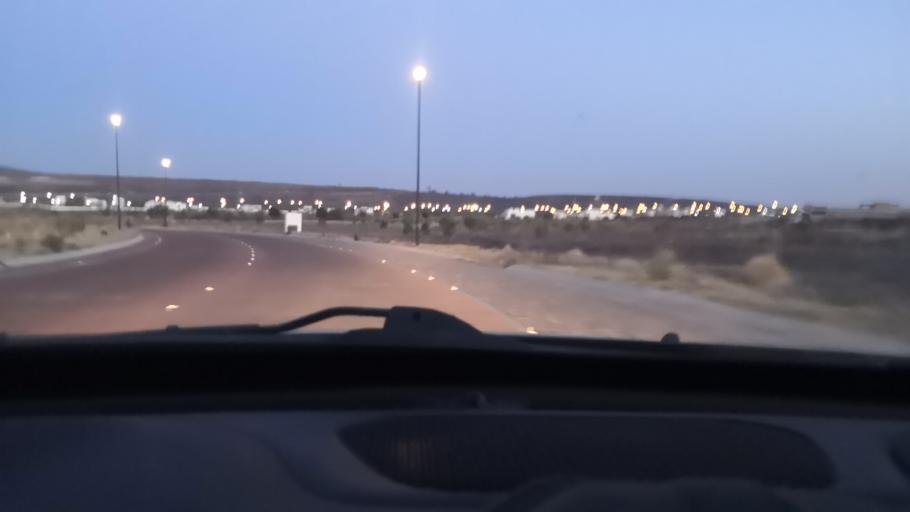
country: MX
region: Guanajuato
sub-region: Leon
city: Fraccionamiento Paseo de las Torres
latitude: 21.2319
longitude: -101.7996
